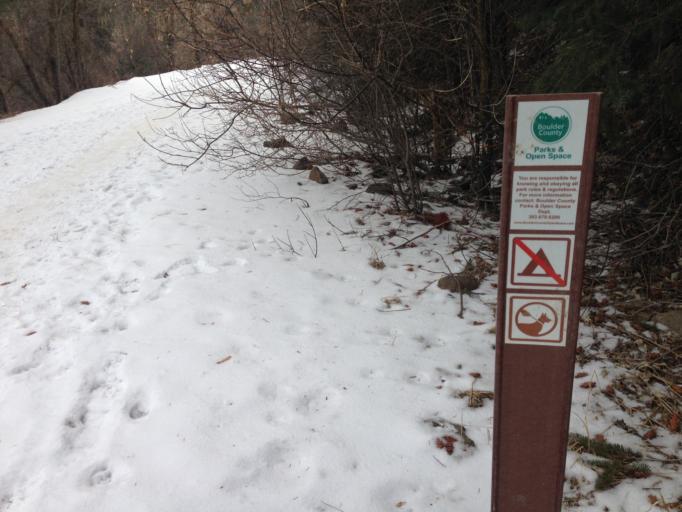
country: US
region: Colorado
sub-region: Boulder County
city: Boulder
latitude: 40.0149
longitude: -105.3250
